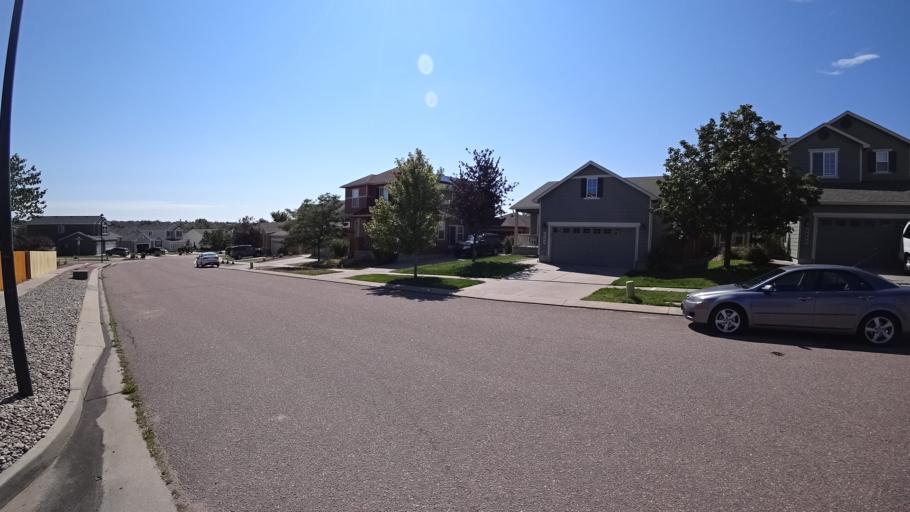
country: US
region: Colorado
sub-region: El Paso County
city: Cimarron Hills
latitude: 38.9185
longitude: -104.7019
